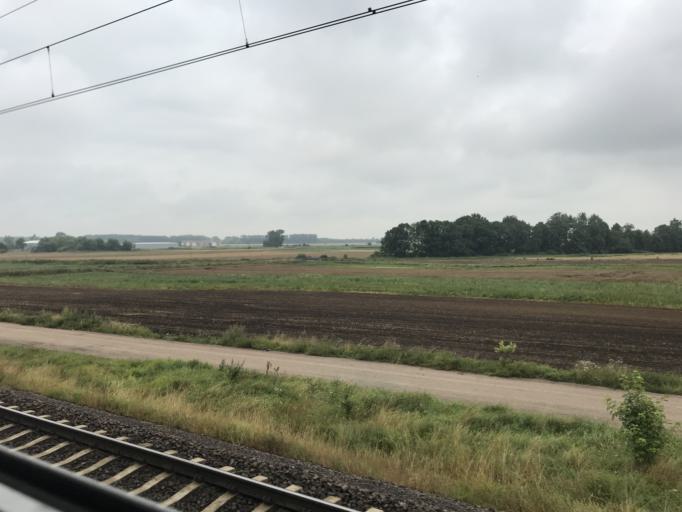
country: PL
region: Pomeranian Voivodeship
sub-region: Powiat gdanski
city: Legowo
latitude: 54.2219
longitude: 18.6534
